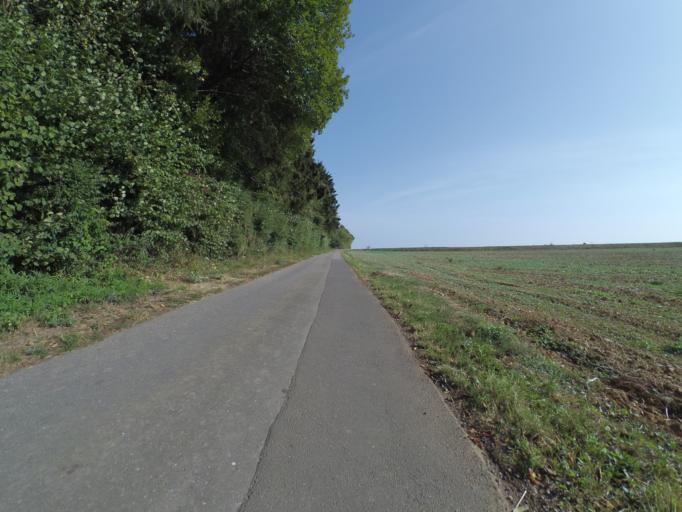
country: DE
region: Rheinland-Pfalz
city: Kirf
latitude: 49.5601
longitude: 6.4766
